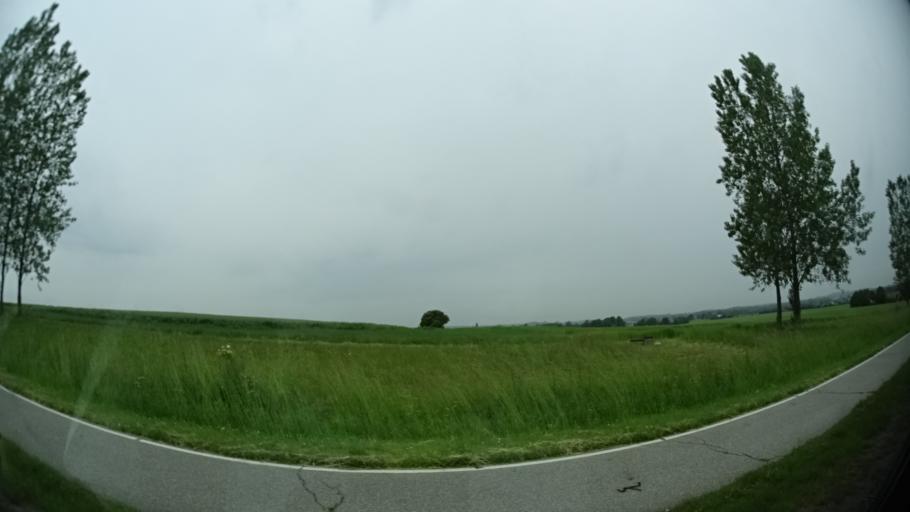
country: DK
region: Central Jutland
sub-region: Arhus Kommune
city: Hjortshoj
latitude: 56.2201
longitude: 10.2851
